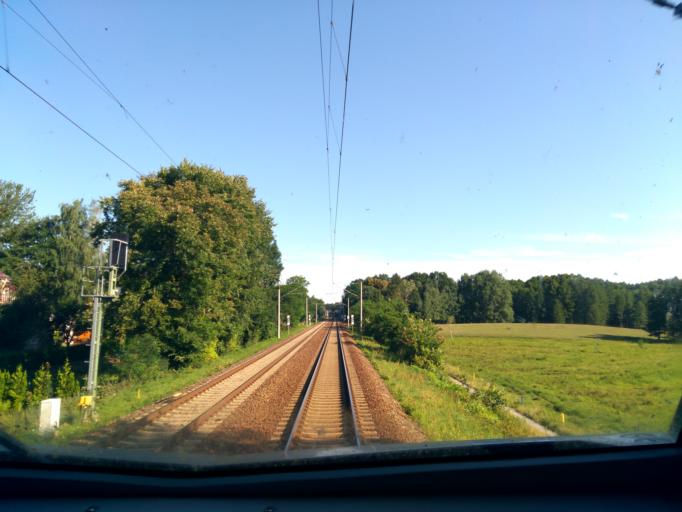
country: DE
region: Brandenburg
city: Halbe
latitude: 52.0910
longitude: 13.7192
